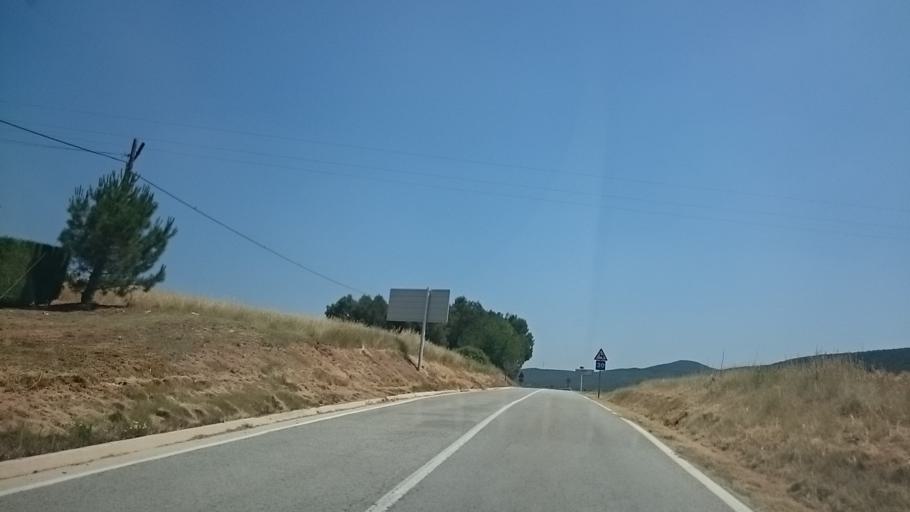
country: ES
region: Catalonia
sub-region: Provincia de Barcelona
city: Sant Marti de Tous
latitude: 41.4909
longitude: 1.5144
